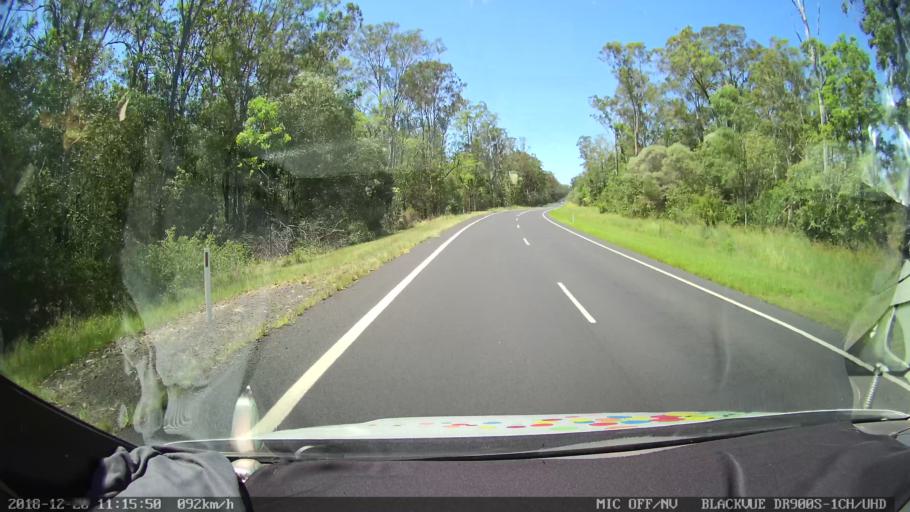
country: AU
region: New South Wales
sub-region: Richmond Valley
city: Casino
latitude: -29.0183
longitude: 153.0109
